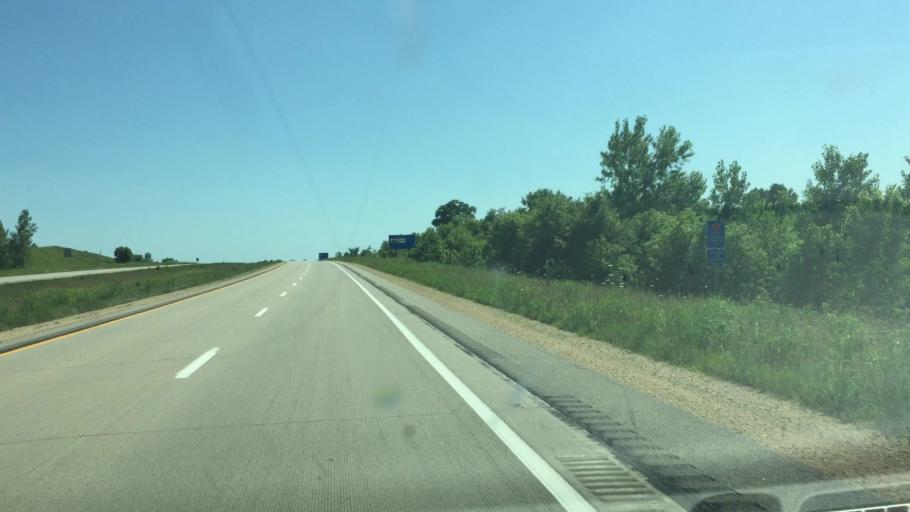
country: US
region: Iowa
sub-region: Jones County
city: Monticello
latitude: 42.2429
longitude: -91.1666
